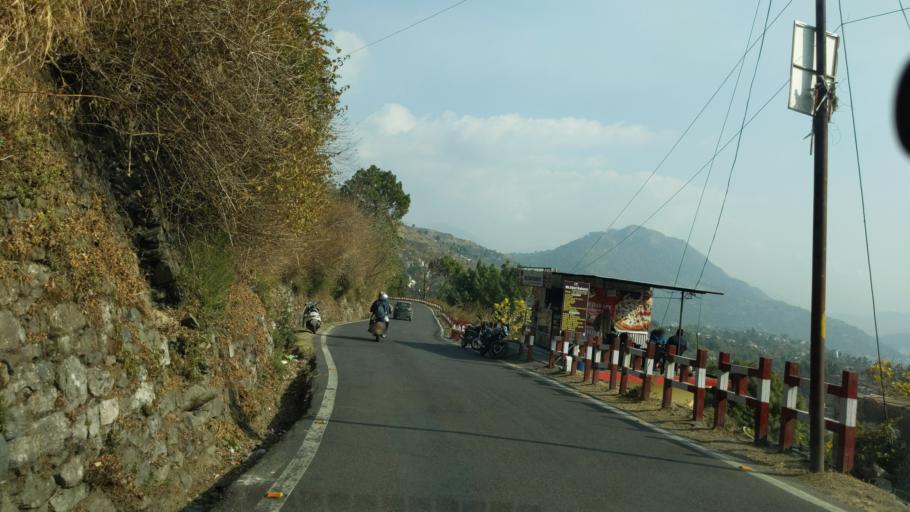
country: IN
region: Uttarakhand
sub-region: Naini Tal
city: Bhowali
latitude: 29.3778
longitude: 79.5281
